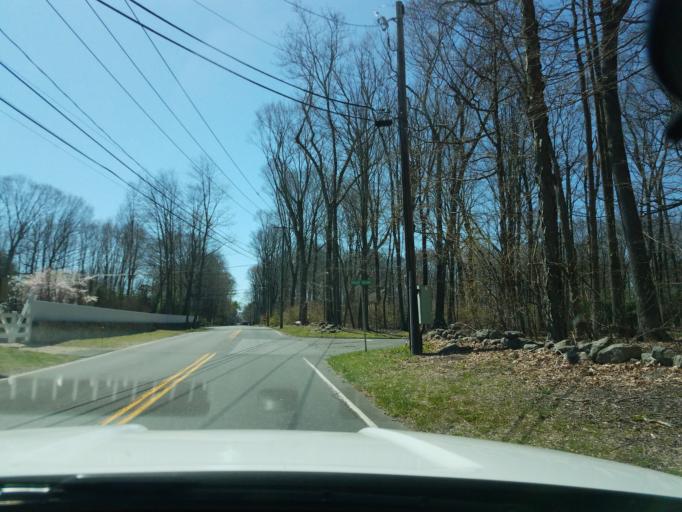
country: US
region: Connecticut
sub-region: Fairfield County
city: Wilton
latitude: 41.2101
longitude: -73.3728
